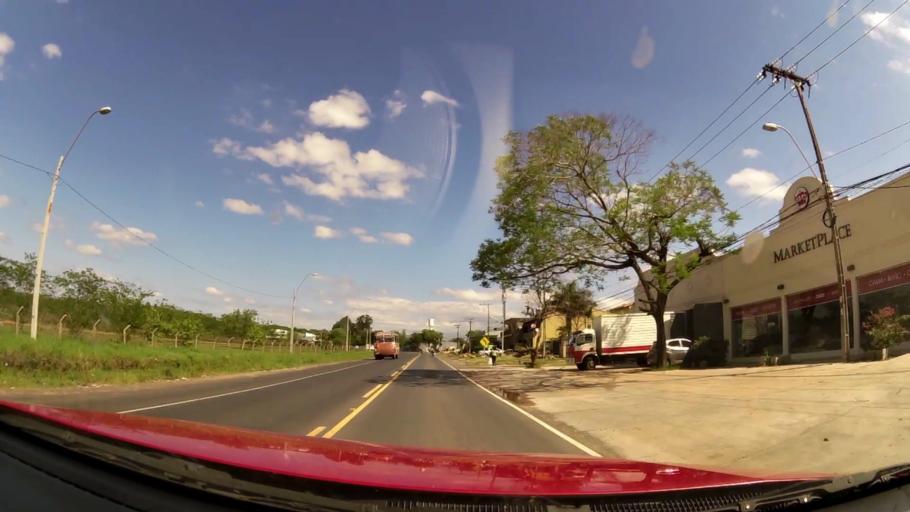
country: PY
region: Central
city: Fernando de la Mora
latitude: -25.2793
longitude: -57.5385
